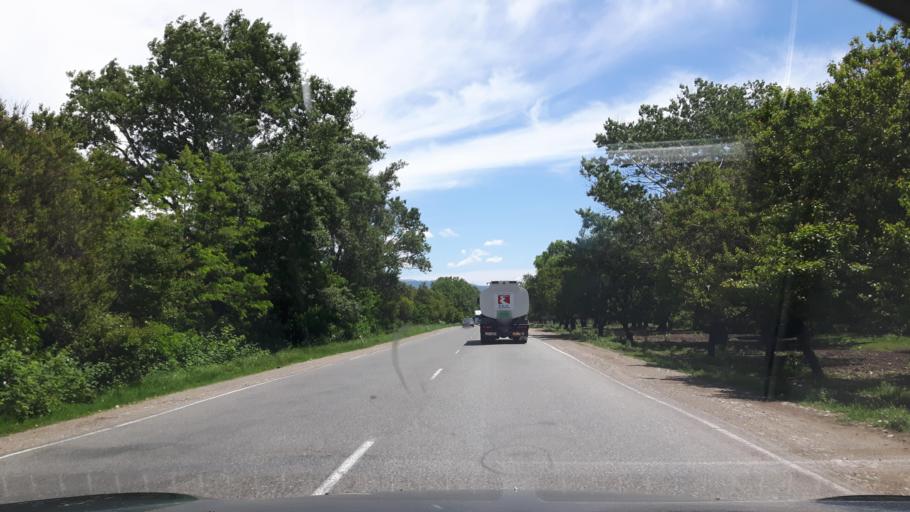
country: GE
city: Didi Lilo
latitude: 41.7101
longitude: 45.1461
